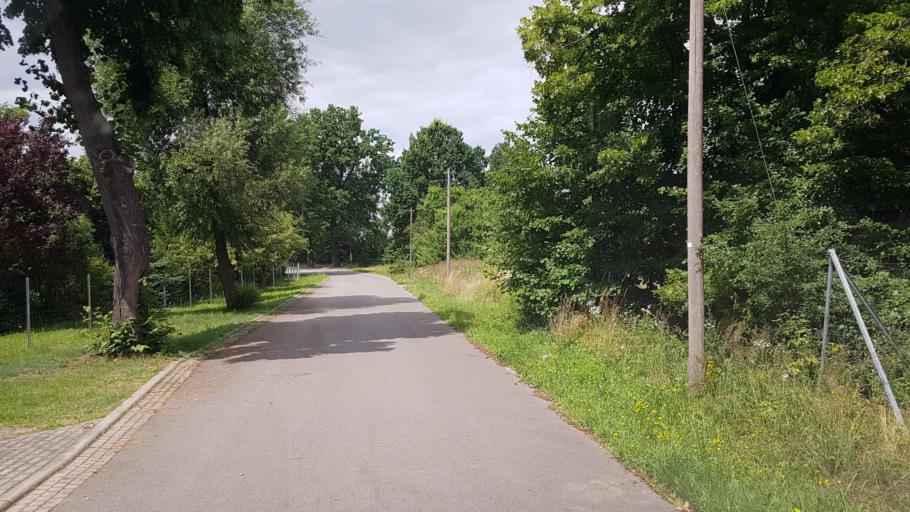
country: DE
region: Brandenburg
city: Altdobern
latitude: 51.6513
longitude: 14.0797
